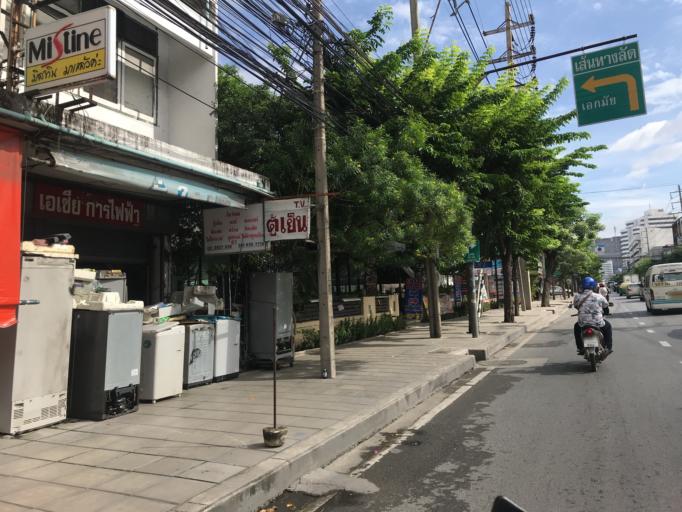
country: TH
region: Bangkok
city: Watthana
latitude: 13.7290
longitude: 100.5961
